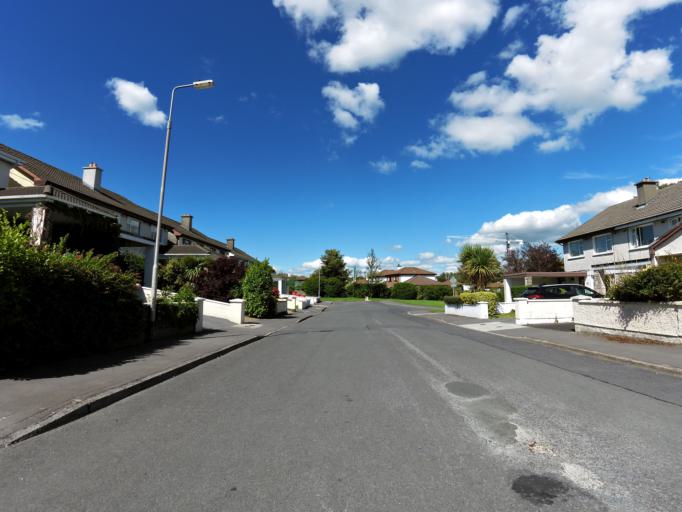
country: IE
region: Connaught
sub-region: County Galway
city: Gaillimh
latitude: 53.2870
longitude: -9.0770
